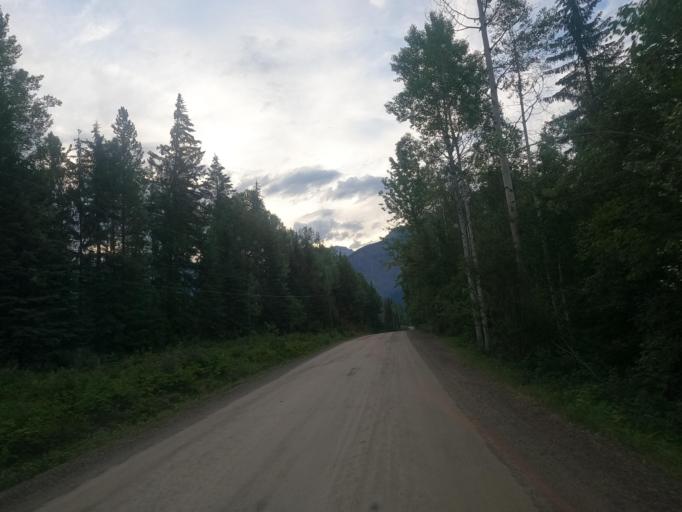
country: CA
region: British Columbia
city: Golden
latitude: 51.4457
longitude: -117.0169
